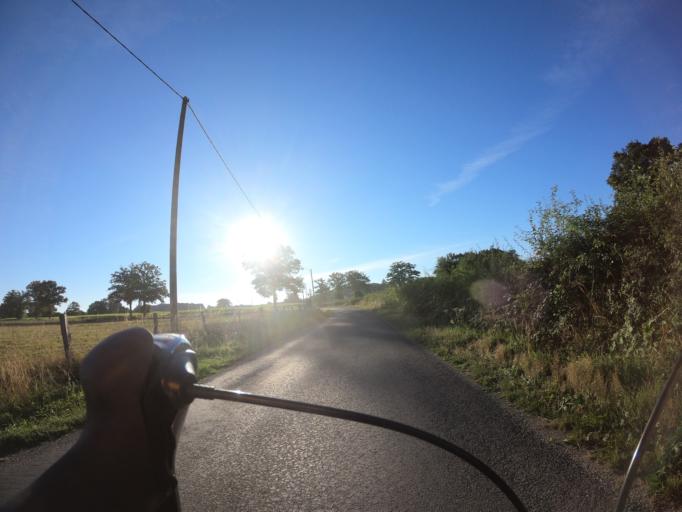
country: FR
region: Lower Normandy
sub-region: Departement de l'Orne
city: Magny-le-Desert
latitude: 48.5384
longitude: -0.2936
